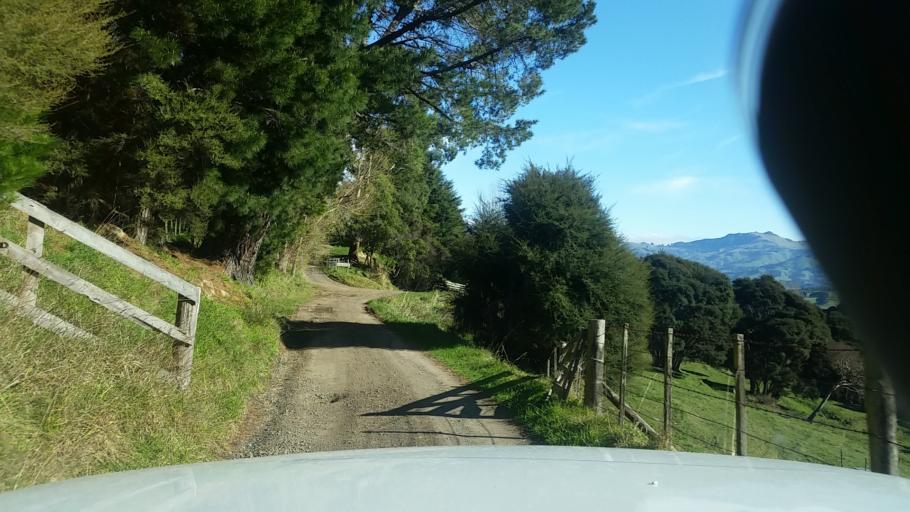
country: NZ
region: Canterbury
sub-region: Christchurch City
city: Christchurch
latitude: -43.7919
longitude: 172.9923
